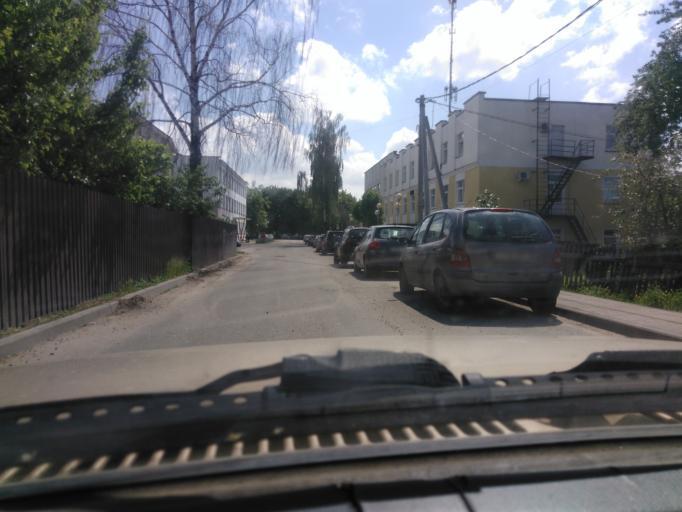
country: BY
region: Mogilev
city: Mahilyow
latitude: 53.9269
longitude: 30.3316
